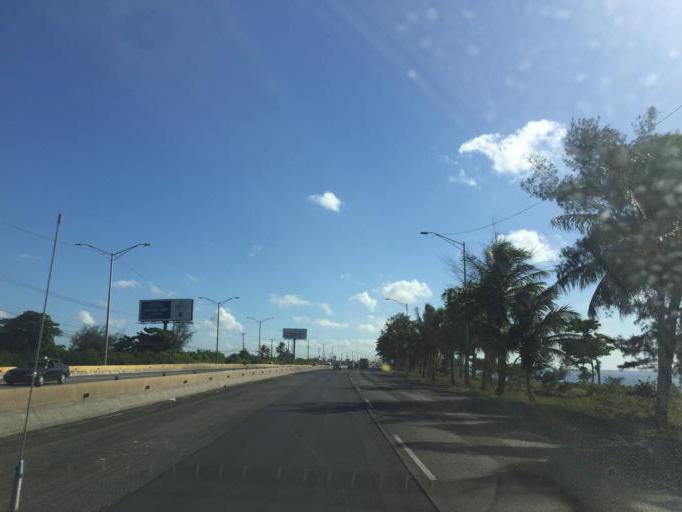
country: DO
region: Santo Domingo
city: Guerra
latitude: 18.4636
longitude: -69.7461
